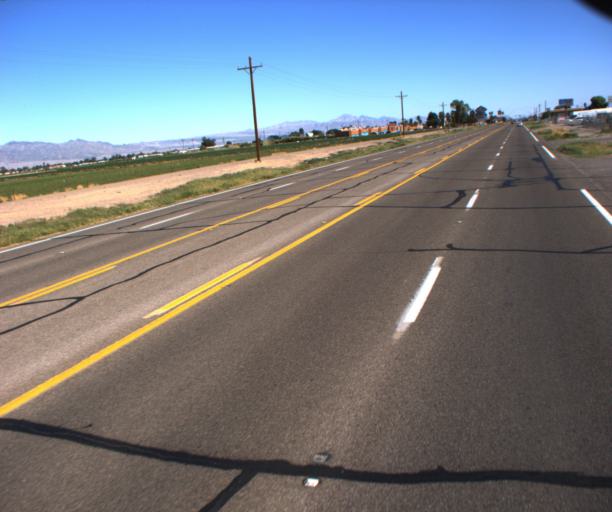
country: US
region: Arizona
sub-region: Mohave County
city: Willow Valley
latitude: 34.9035
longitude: -114.5978
